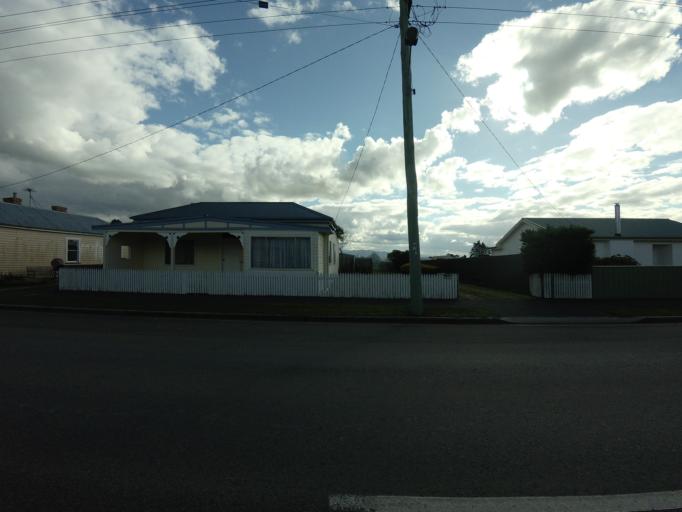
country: AU
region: Tasmania
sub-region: Northern Midlands
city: Longford
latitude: -41.6883
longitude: 147.0798
